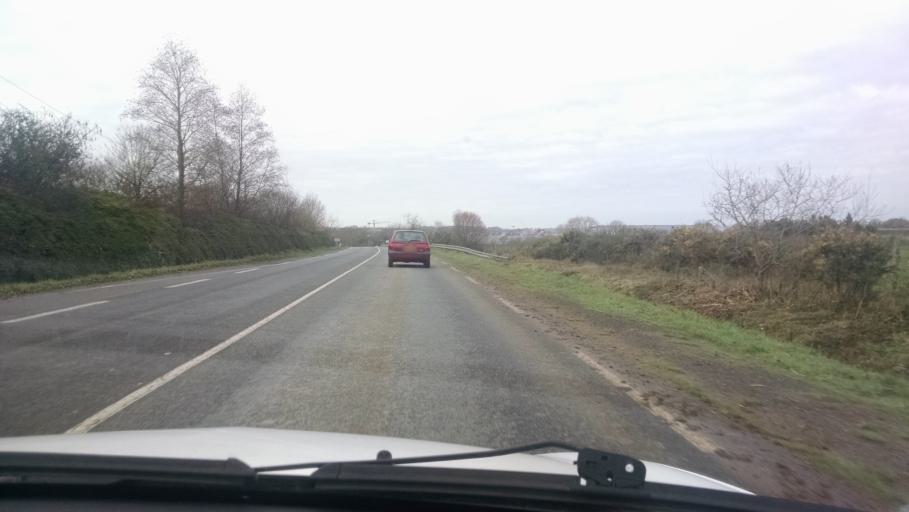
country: FR
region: Pays de la Loire
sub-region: Departement de Maine-et-Loire
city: La Romagne
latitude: 47.0586
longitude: -0.9990
